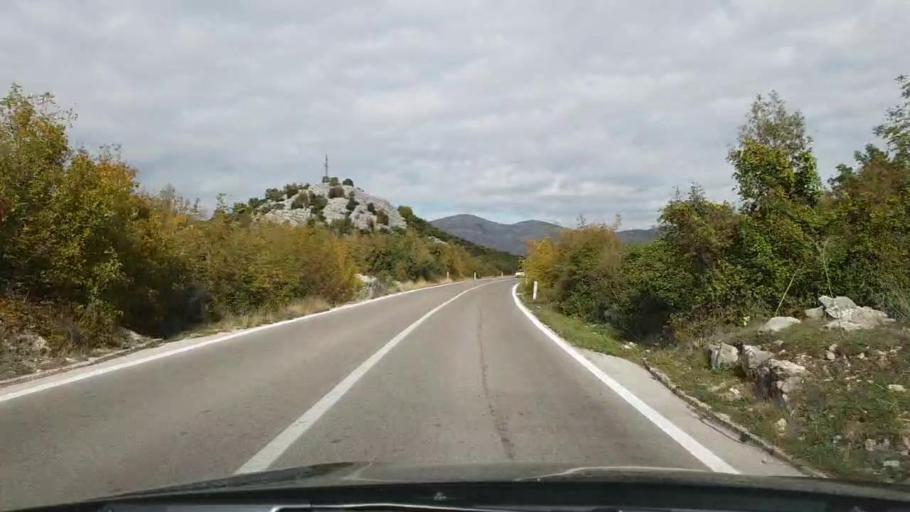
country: HR
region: Dubrovacko-Neretvanska
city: Cibaca
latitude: 42.6823
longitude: 18.2457
